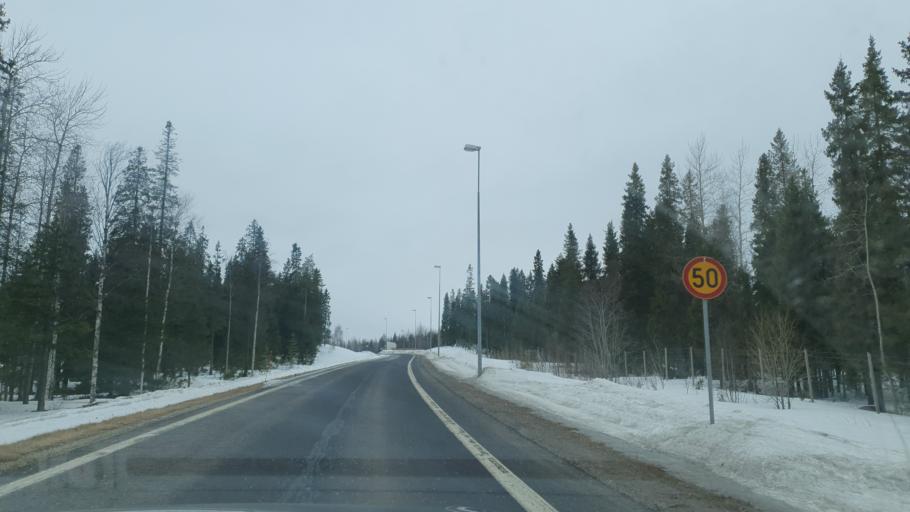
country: FI
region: Lapland
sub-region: Kemi-Tornio
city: Keminmaa
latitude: 65.8261
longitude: 24.4152
